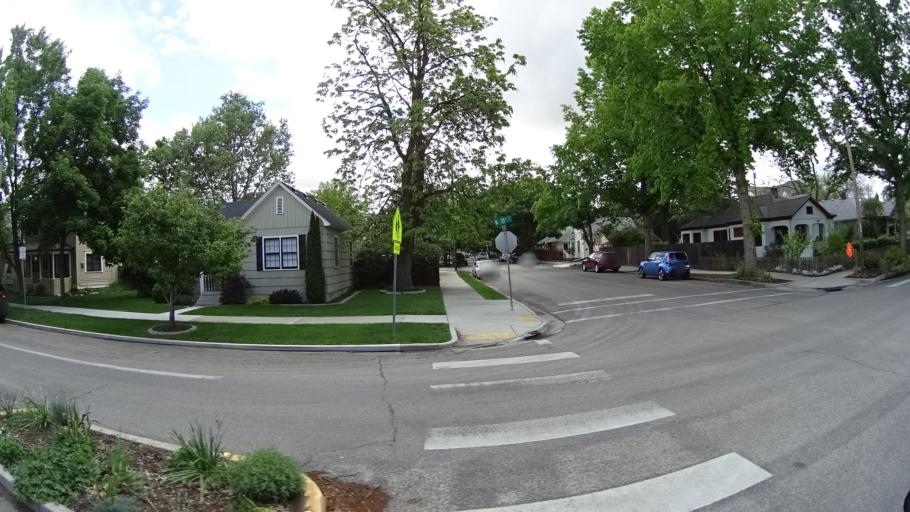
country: US
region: Idaho
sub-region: Ada County
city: Boise
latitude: 43.6313
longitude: -116.2059
